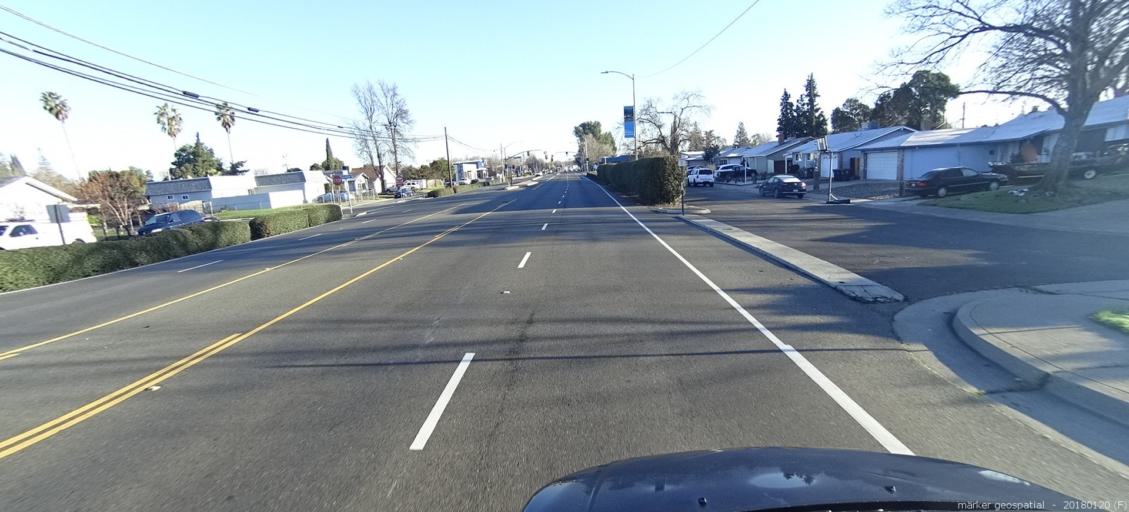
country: US
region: California
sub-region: Sacramento County
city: Rancho Cordova
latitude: 38.6099
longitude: -121.2923
